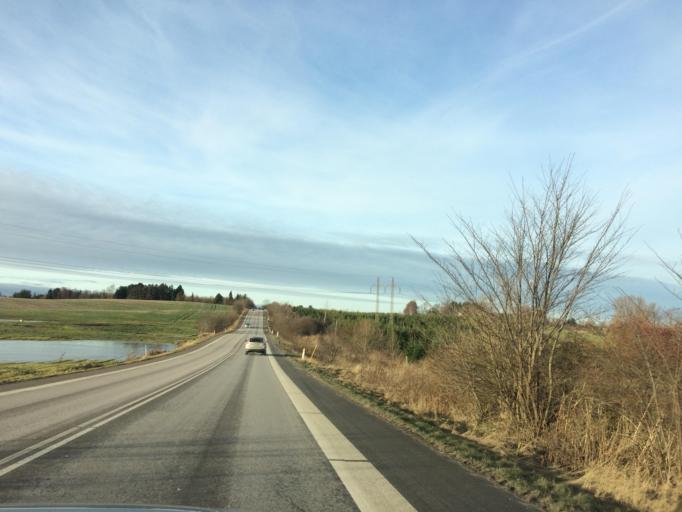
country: DK
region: Capital Region
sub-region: Fredensborg Kommune
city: Kokkedal
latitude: 55.9102
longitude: 12.4669
